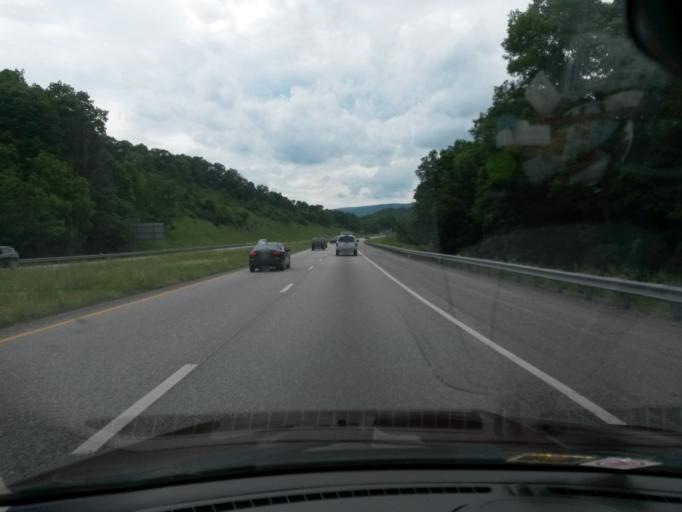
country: US
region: Virginia
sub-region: Alleghany County
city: Clifton Forge
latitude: 37.8279
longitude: -79.8005
